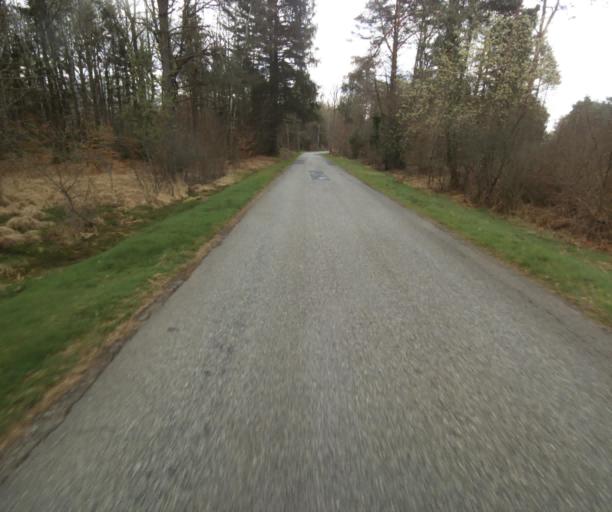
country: FR
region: Limousin
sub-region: Departement de la Correze
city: Correze
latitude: 45.2487
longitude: 1.9339
